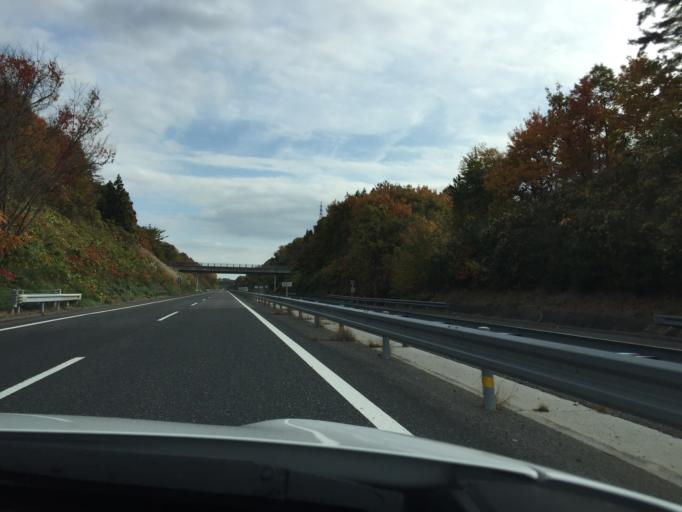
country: JP
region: Fukushima
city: Funehikimachi-funehiki
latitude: 37.4121
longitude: 140.5641
